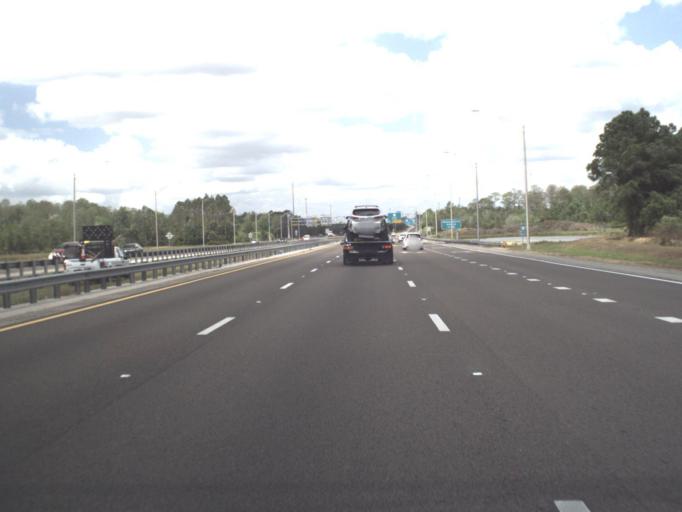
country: US
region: Florida
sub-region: Orange County
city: Alafaya
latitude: 28.4516
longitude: -81.2154
